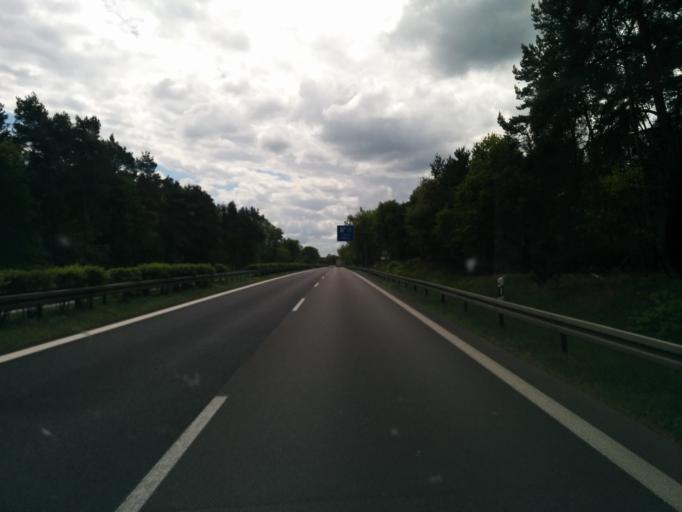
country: DE
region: Brandenburg
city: Werder
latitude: 52.4450
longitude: 12.9325
